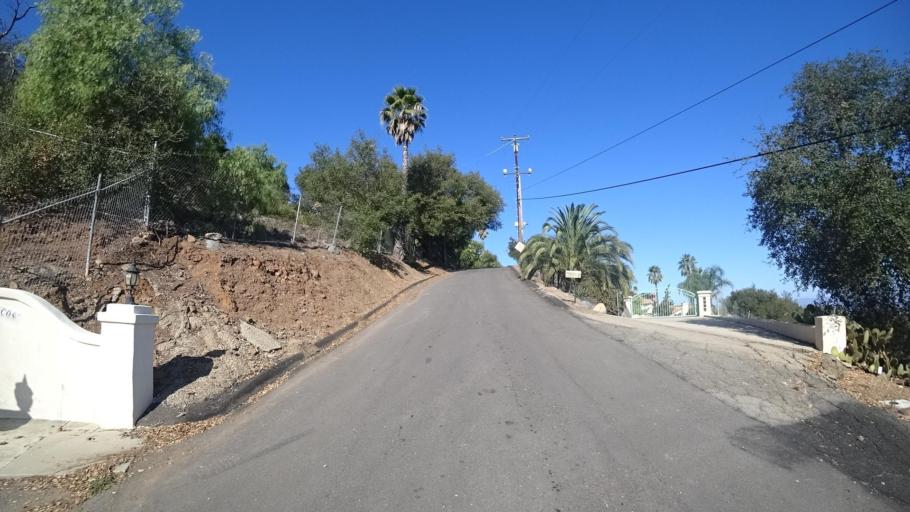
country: US
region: California
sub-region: San Diego County
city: Hidden Meadows
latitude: 33.2362
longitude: -117.1212
